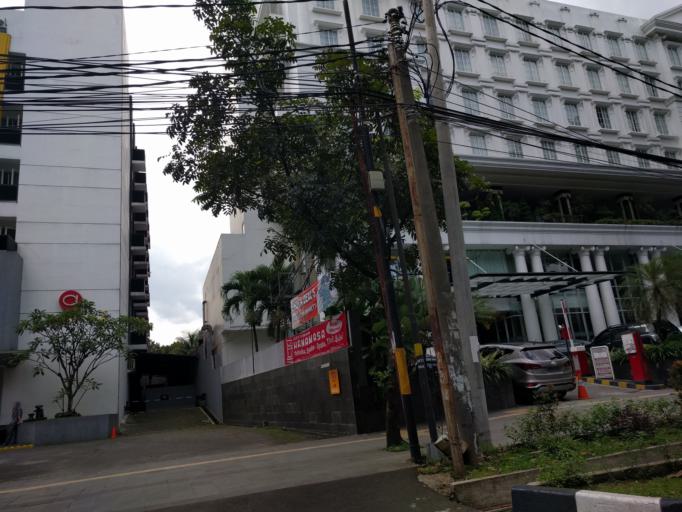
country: ID
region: West Java
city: Bogor
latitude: -6.5964
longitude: 106.8045
